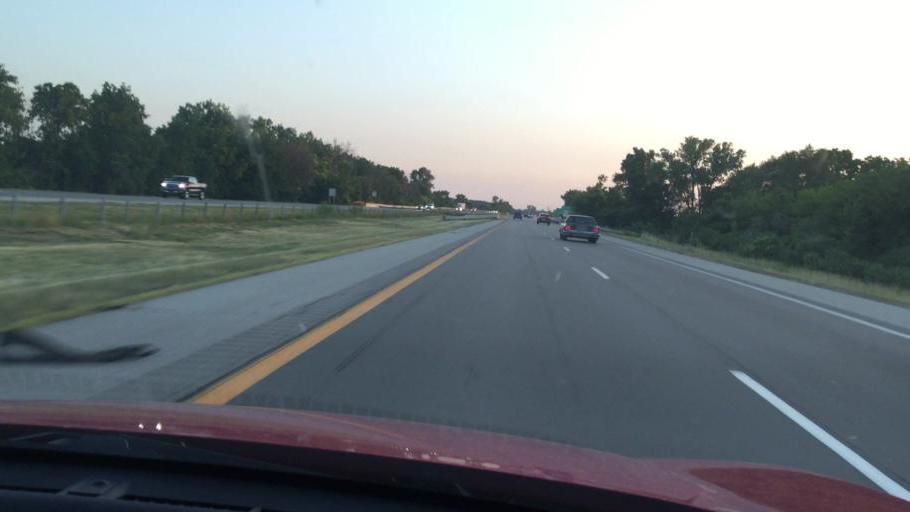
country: US
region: Michigan
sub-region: Washtenaw County
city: Milan
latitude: 42.0239
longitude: -83.6786
